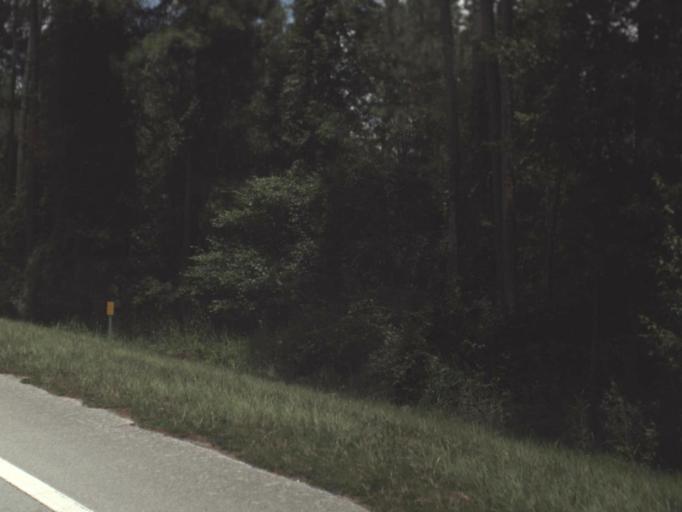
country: US
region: Florida
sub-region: Baker County
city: Macclenny
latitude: 30.1448
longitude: -82.1859
